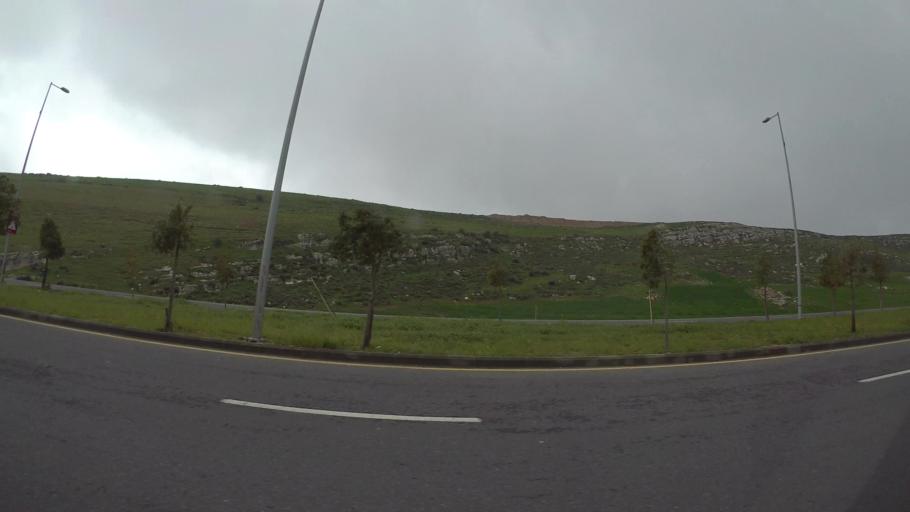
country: JO
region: Amman
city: Al Bunayyat ash Shamaliyah
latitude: 31.9308
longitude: 35.8766
